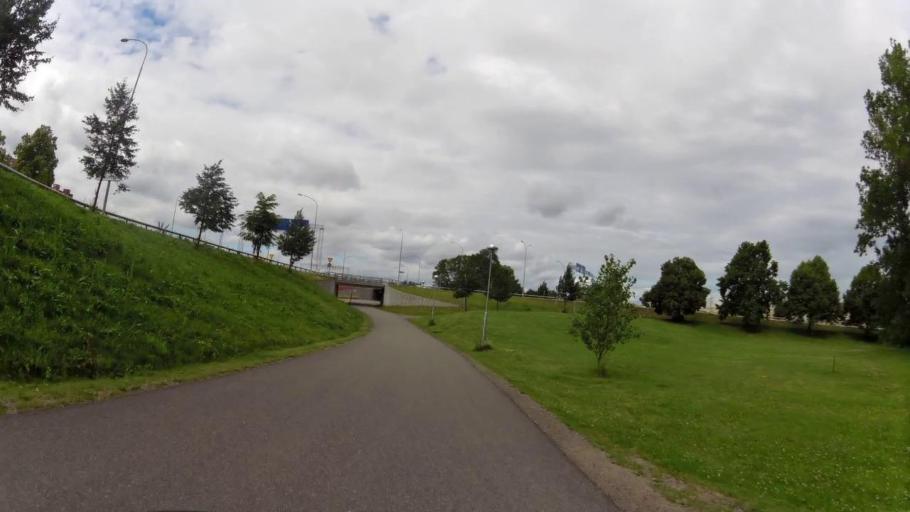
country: SE
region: OEstergoetland
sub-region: Linkopings Kommun
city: Linkoping
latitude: 58.4192
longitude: 15.5983
